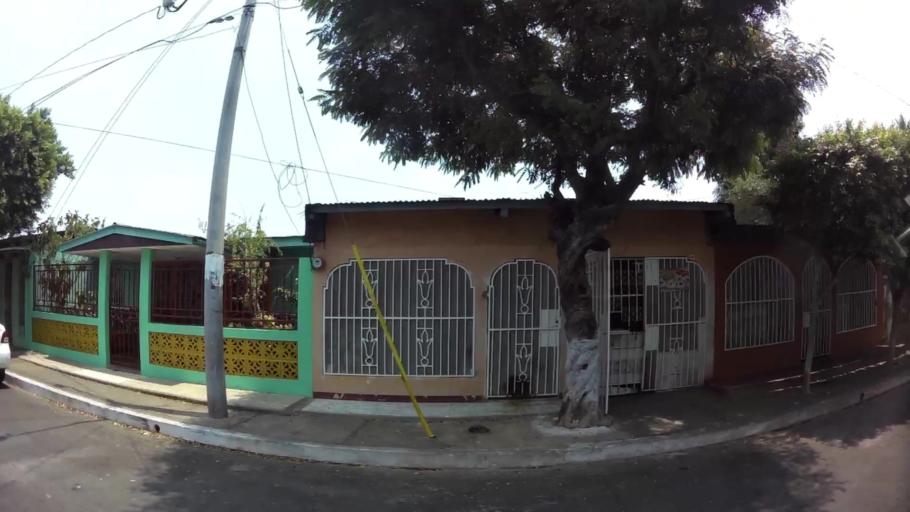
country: NI
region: Managua
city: Ciudad Sandino
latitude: 12.1486
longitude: -86.3005
